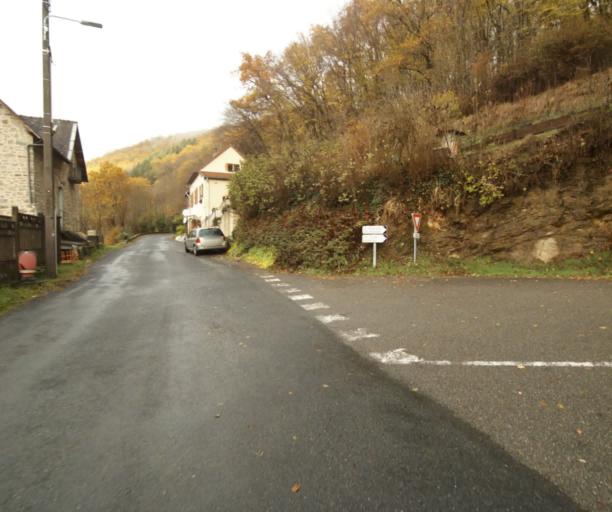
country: FR
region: Limousin
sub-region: Departement de la Correze
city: Cornil
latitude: 45.1812
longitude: 1.6471
